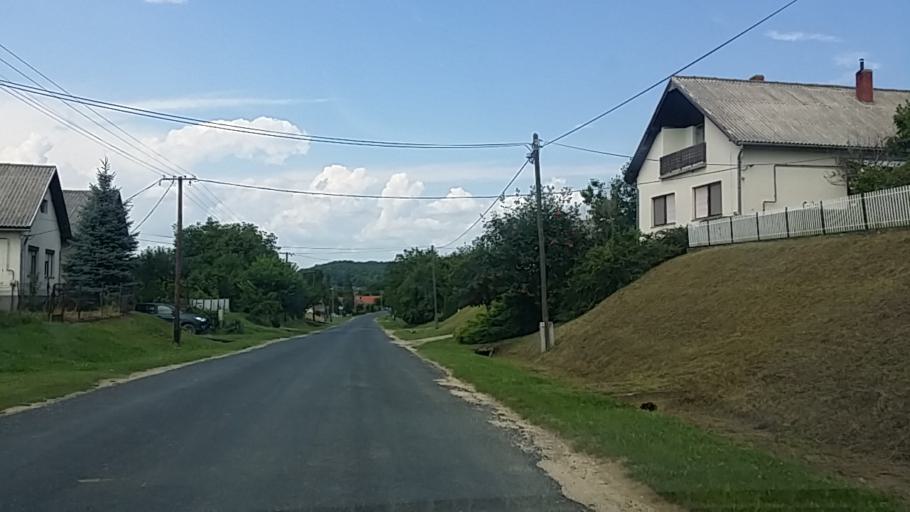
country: HR
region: Medimurska
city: Podturen
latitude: 46.5328
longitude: 16.5885
